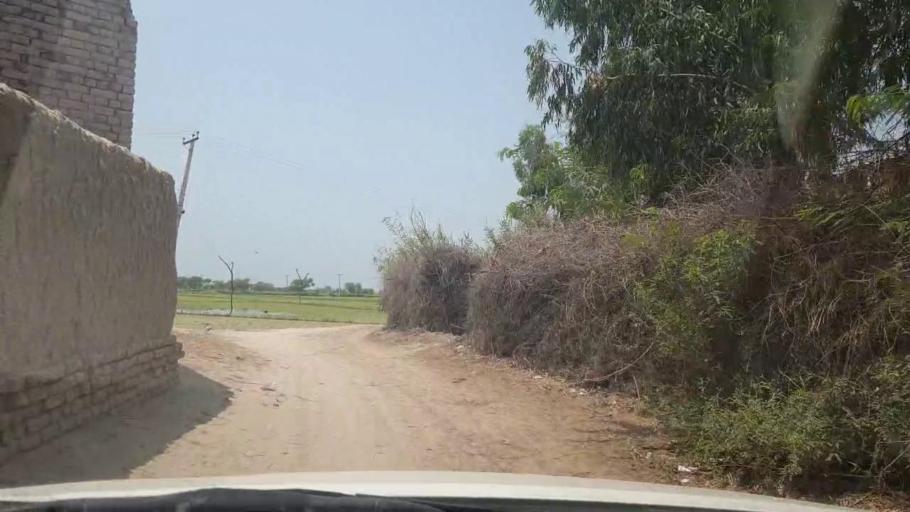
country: PK
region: Sindh
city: Rustam jo Goth
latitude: 28.0428
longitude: 68.7527
